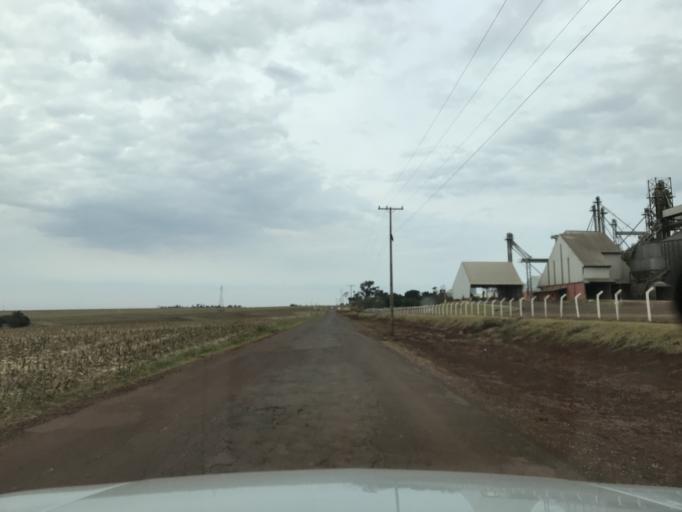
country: BR
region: Parana
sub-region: Palotina
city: Palotina
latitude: -24.2848
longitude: -53.7986
